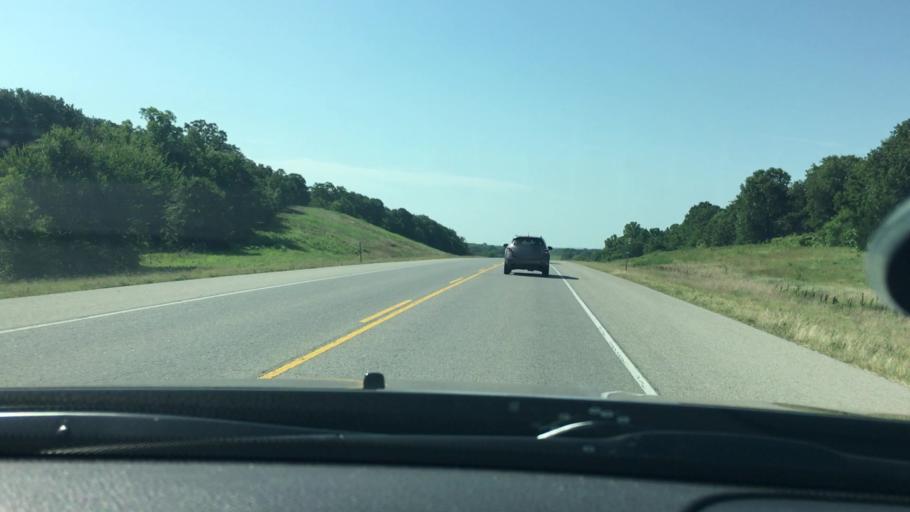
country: US
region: Oklahoma
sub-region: Pontotoc County
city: Ada
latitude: 34.6698
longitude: -96.5686
